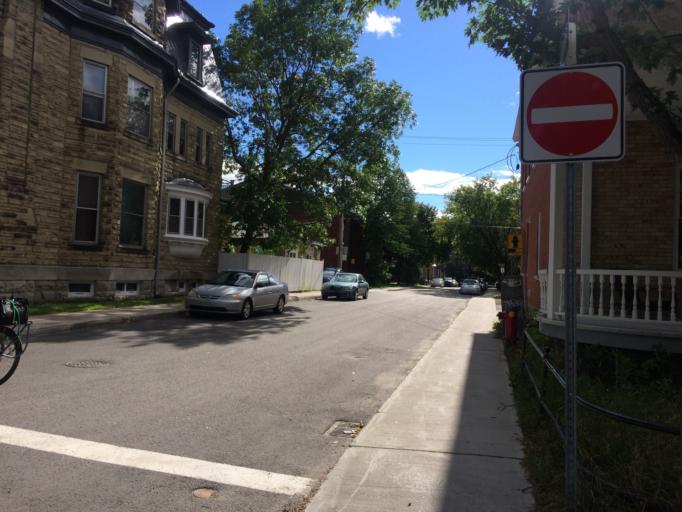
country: CA
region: Quebec
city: Quebec
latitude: 46.8031
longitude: -71.2305
